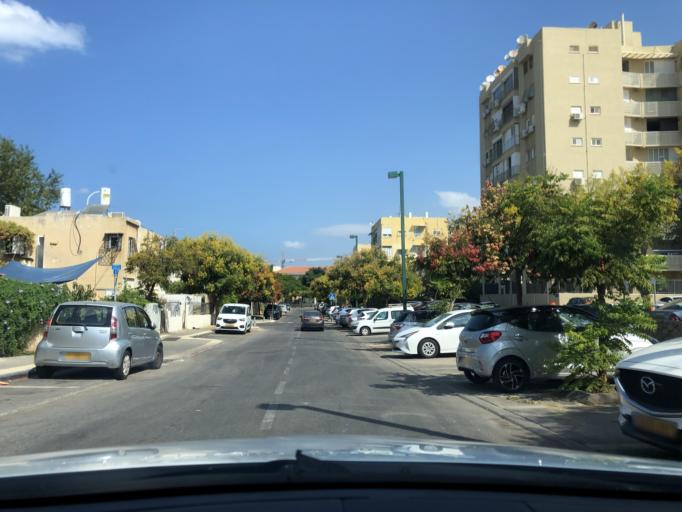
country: IL
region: Tel Aviv
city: Yafo
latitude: 32.0422
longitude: 34.7563
